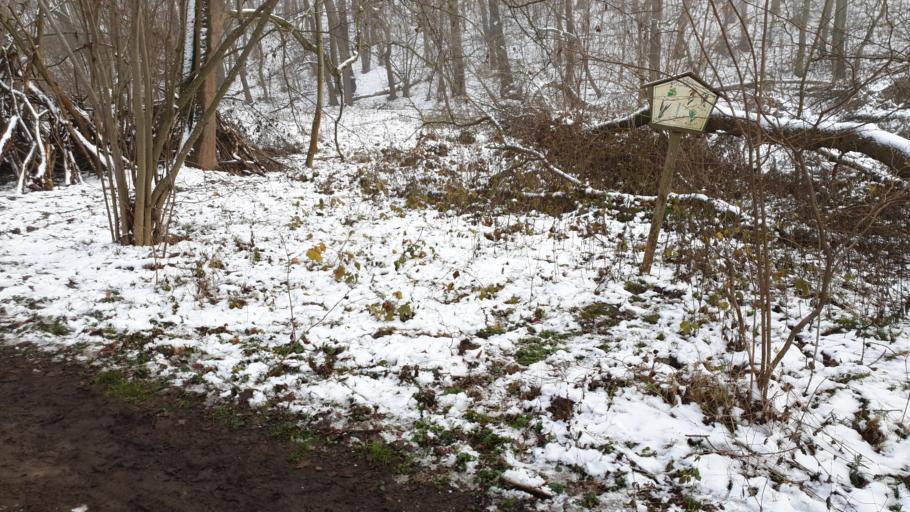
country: DE
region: Saxony
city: Taucha
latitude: 51.4008
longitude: 12.4937
